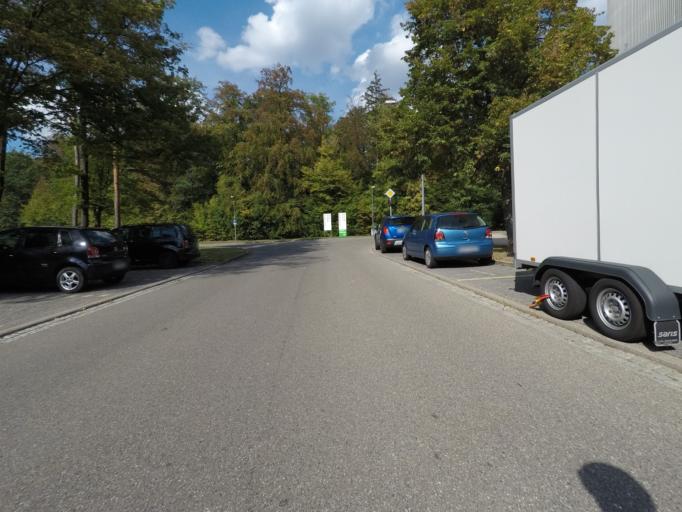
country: DE
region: Baden-Wuerttemberg
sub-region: Regierungsbezirk Stuttgart
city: Gerlingen
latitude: 48.7503
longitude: 9.1099
